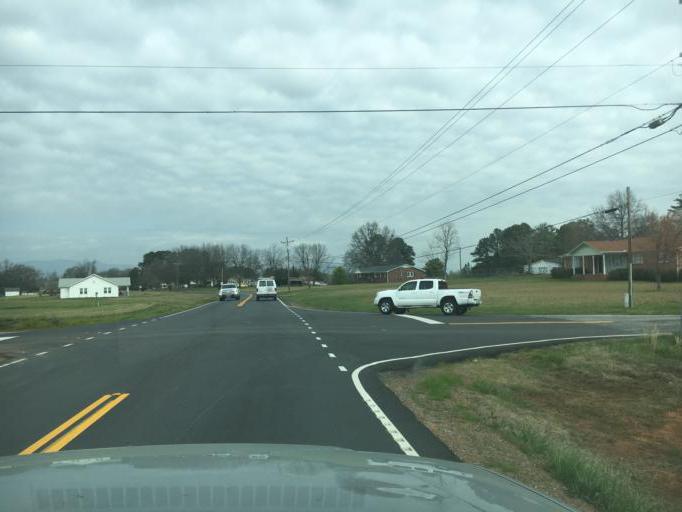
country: US
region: South Carolina
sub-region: Spartanburg County
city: Inman Mills
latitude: 35.0497
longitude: -82.1388
